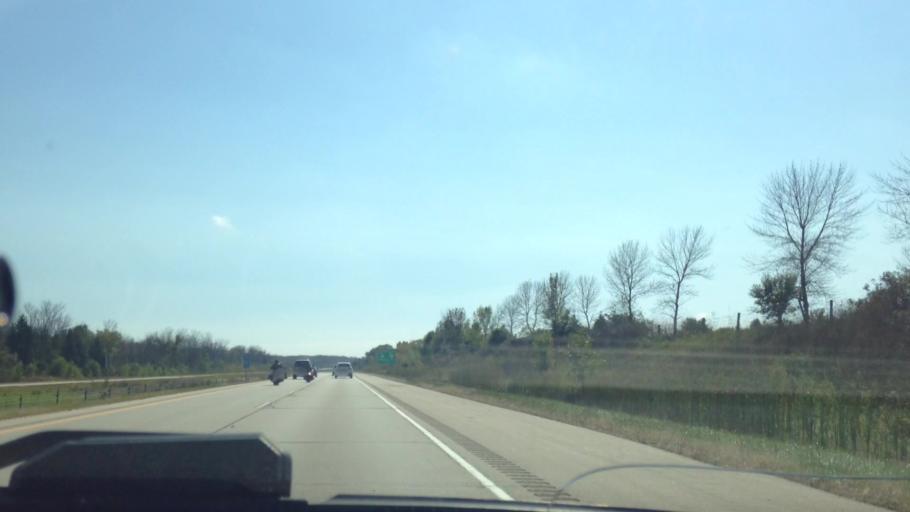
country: US
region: Wisconsin
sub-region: Ozaukee County
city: Thiensville
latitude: 43.2421
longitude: -87.9201
